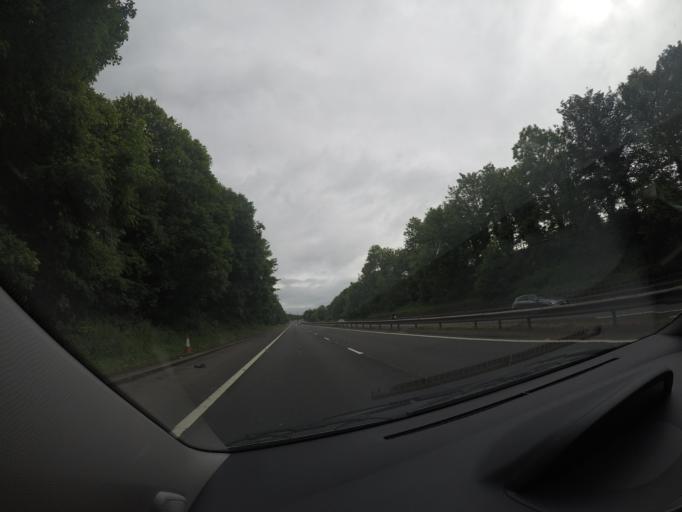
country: GB
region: Scotland
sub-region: Falkirk
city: Dunipace
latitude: 56.0276
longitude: -3.9233
